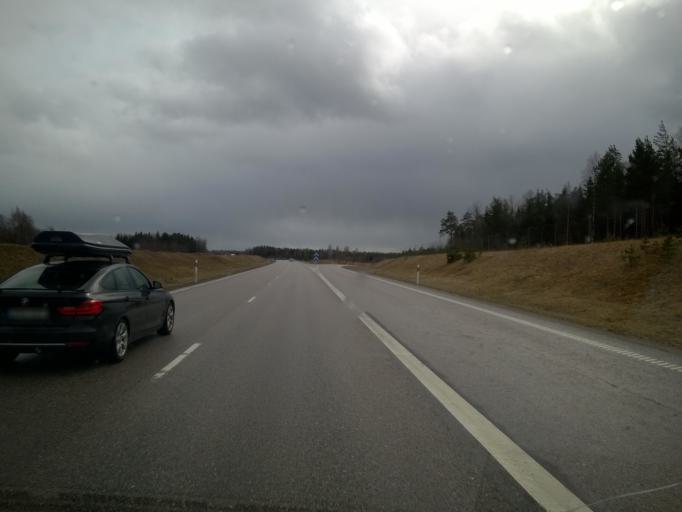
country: SE
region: Uppsala
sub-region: Osthammars Kommun
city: Bjorklinge
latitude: 60.0155
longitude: 17.6235
